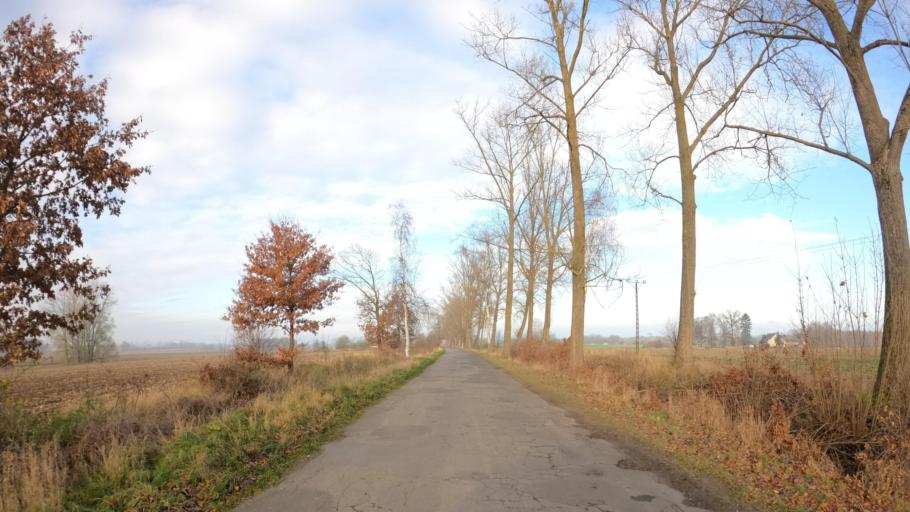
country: PL
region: West Pomeranian Voivodeship
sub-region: Powiat goleniowski
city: Maszewo
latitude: 53.5671
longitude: 15.0908
